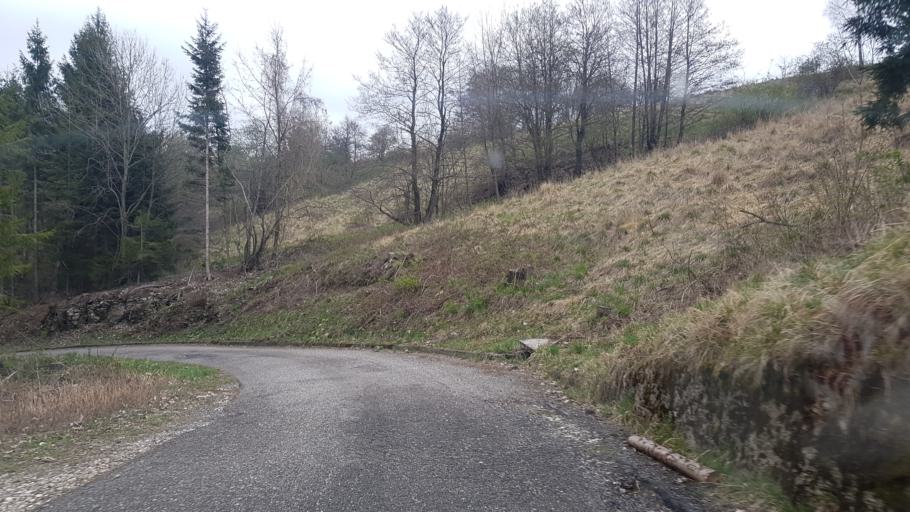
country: IT
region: Friuli Venezia Giulia
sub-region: Provincia di Udine
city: Torreano
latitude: 46.1711
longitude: 13.4111
